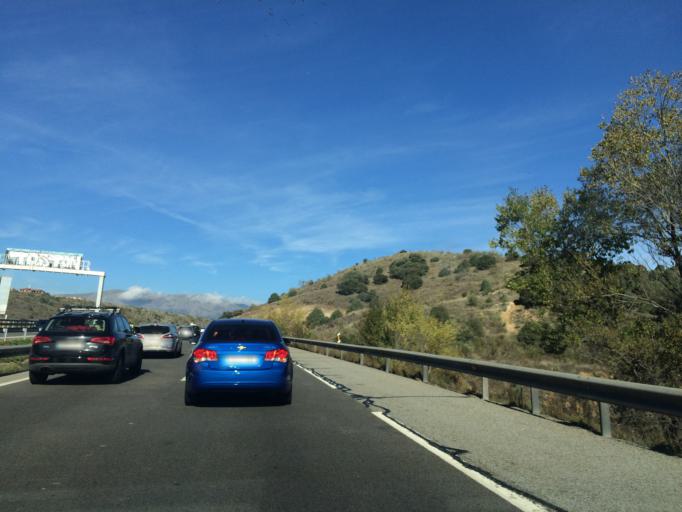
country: ES
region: Madrid
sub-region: Provincia de Madrid
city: Venturada
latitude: 40.8019
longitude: -3.6163
